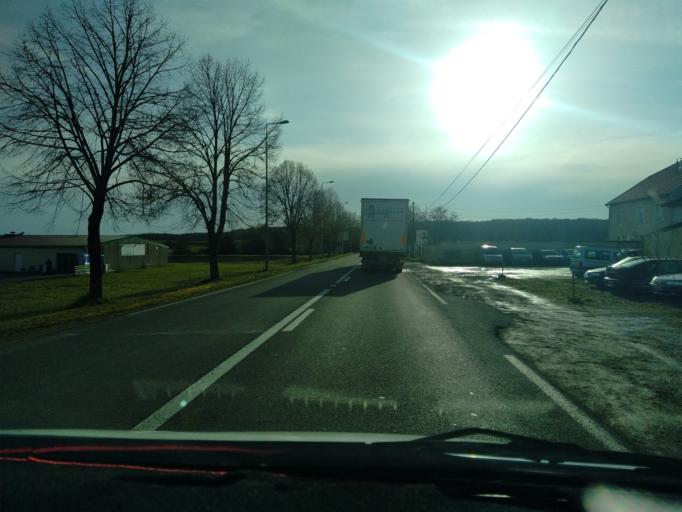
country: FR
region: Franche-Comte
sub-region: Departement de la Haute-Saone
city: Gray
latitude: 47.4333
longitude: 5.6021
